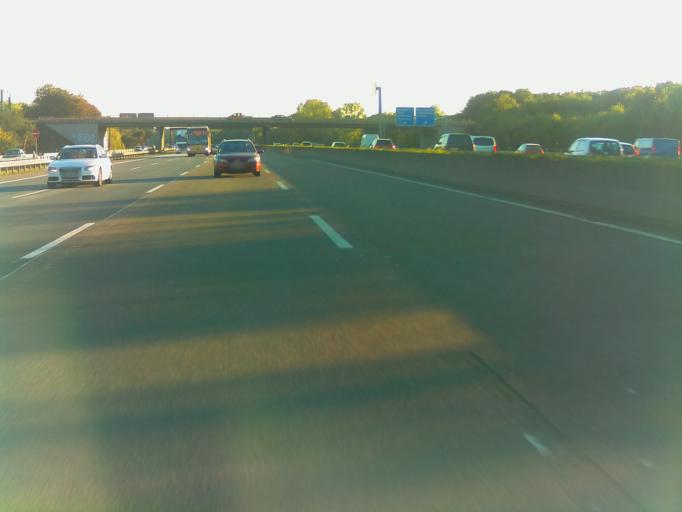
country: DE
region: Hesse
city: Morfelden-Walldorf
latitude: 50.0367
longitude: 8.5962
